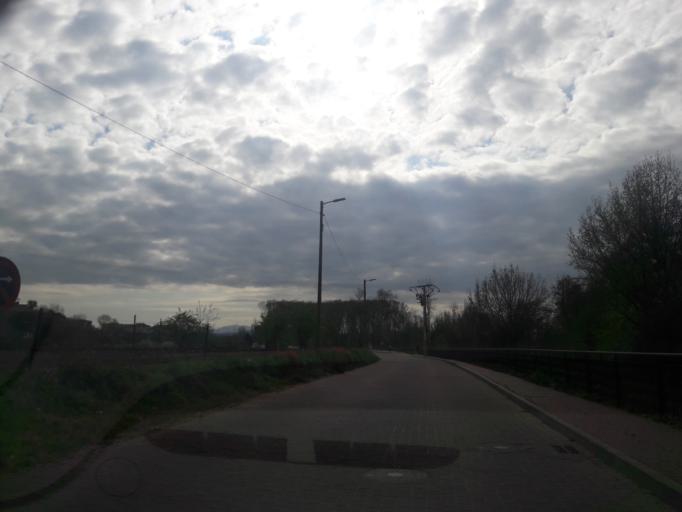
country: ES
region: Castille and Leon
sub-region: Provincia de Salamanca
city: Ciudad Rodrigo
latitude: 40.5943
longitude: -6.5325
